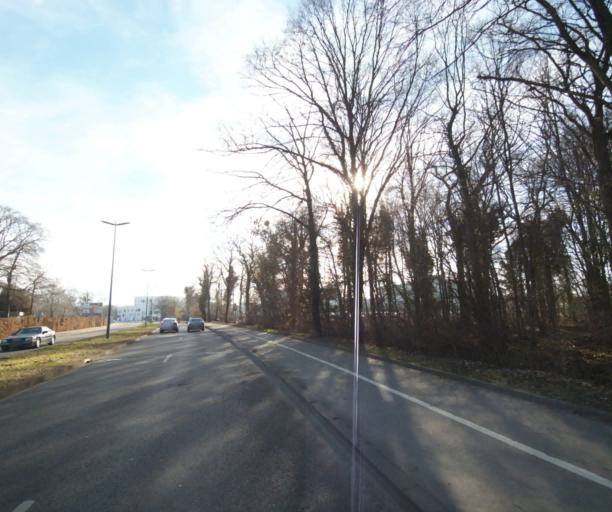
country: FR
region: Lorraine
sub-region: Departement de Meurthe-et-Moselle
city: Villers-les-Nancy
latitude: 48.6514
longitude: 6.1386
